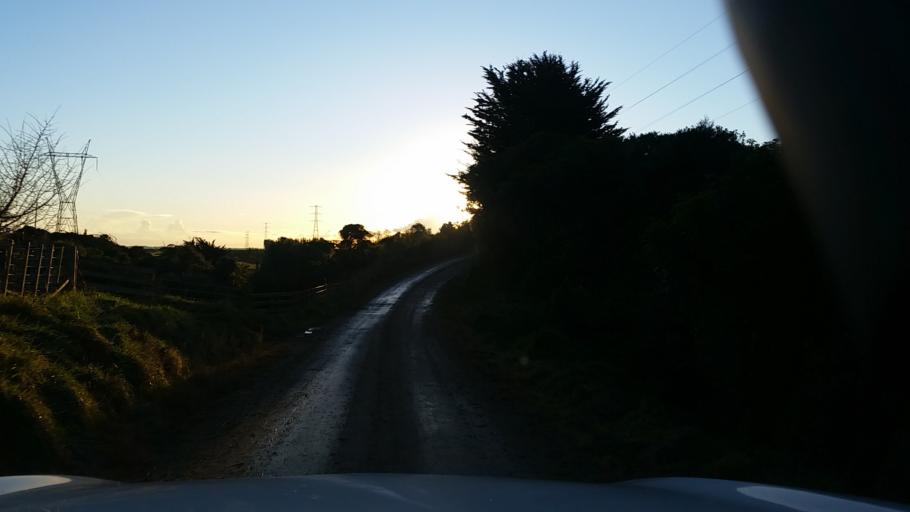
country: NZ
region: Manawatu-Wanganui
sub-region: Wanganui District
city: Wanganui
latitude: -39.8006
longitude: 174.8032
